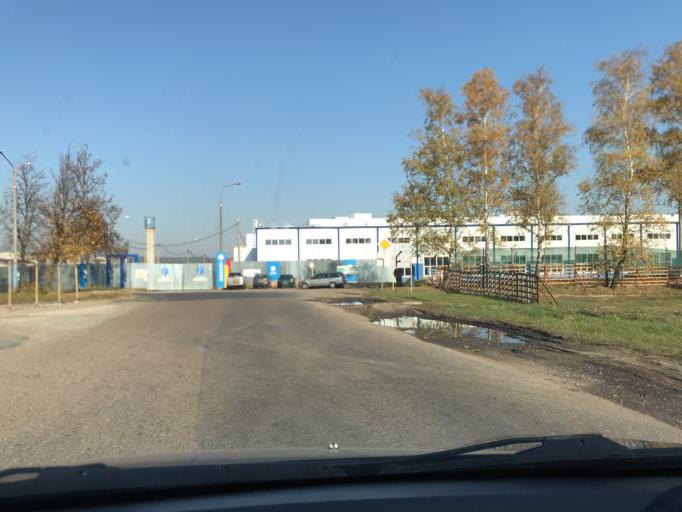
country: BY
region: Minsk
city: Pryvol'ny
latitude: 53.8100
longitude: 27.7844
